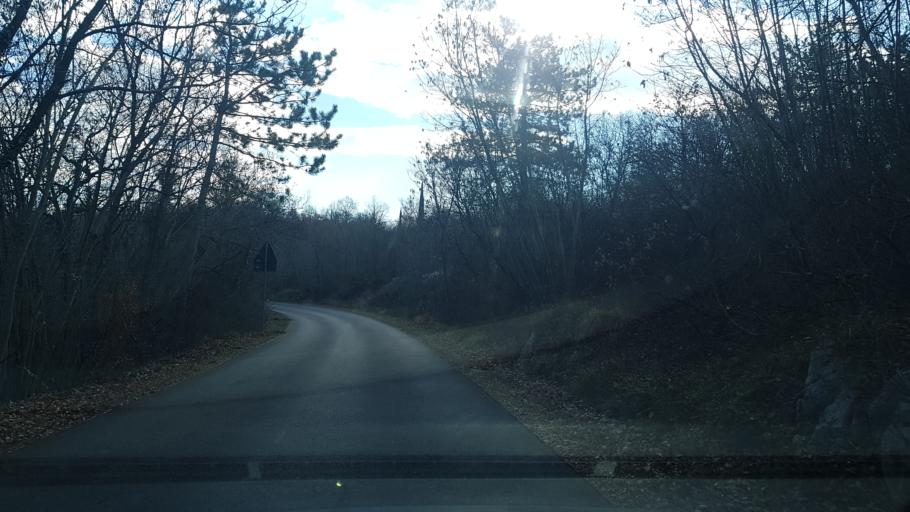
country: IT
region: Friuli Venezia Giulia
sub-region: Provincia di Gorizia
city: Gradisca d'Isonzo
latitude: 45.8778
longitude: 13.5268
